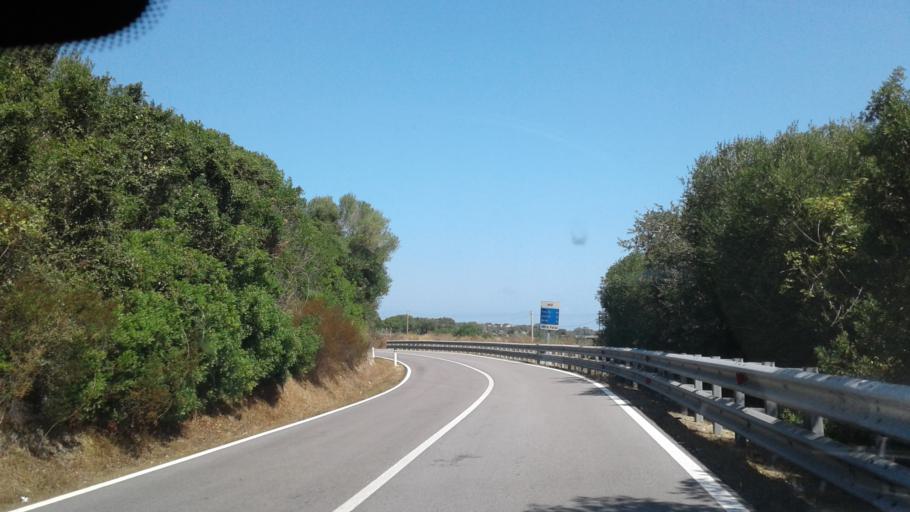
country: IT
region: Sardinia
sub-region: Provincia di Olbia-Tempio
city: Palau
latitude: 41.1578
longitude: 9.3155
